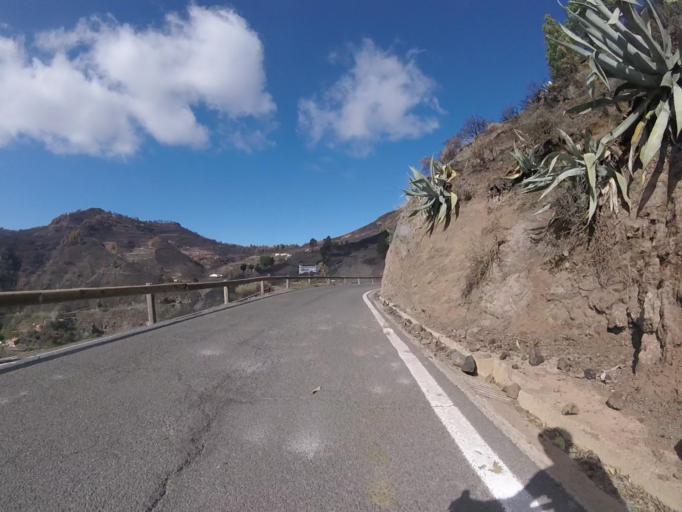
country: ES
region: Canary Islands
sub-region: Provincia de Las Palmas
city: Tejeda
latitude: 28.0091
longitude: -15.5877
